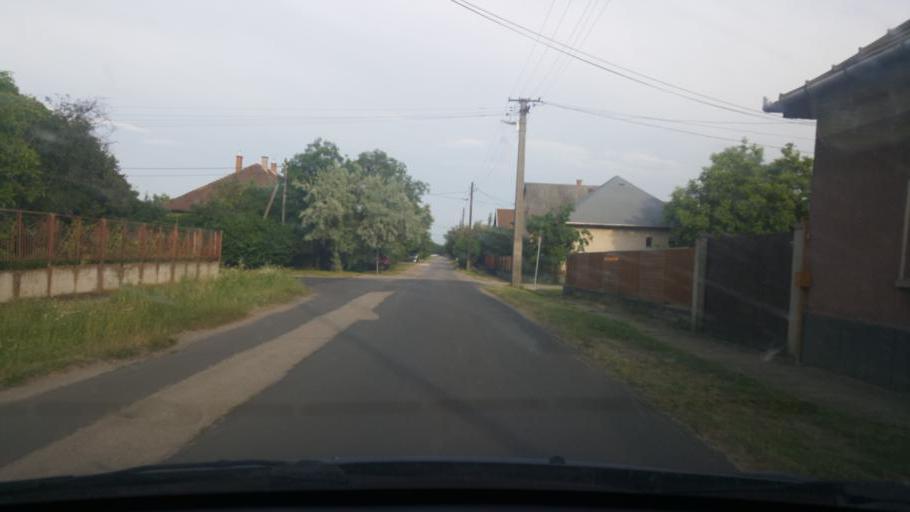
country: HU
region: Pest
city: Monor
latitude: 47.3387
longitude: 19.4474
